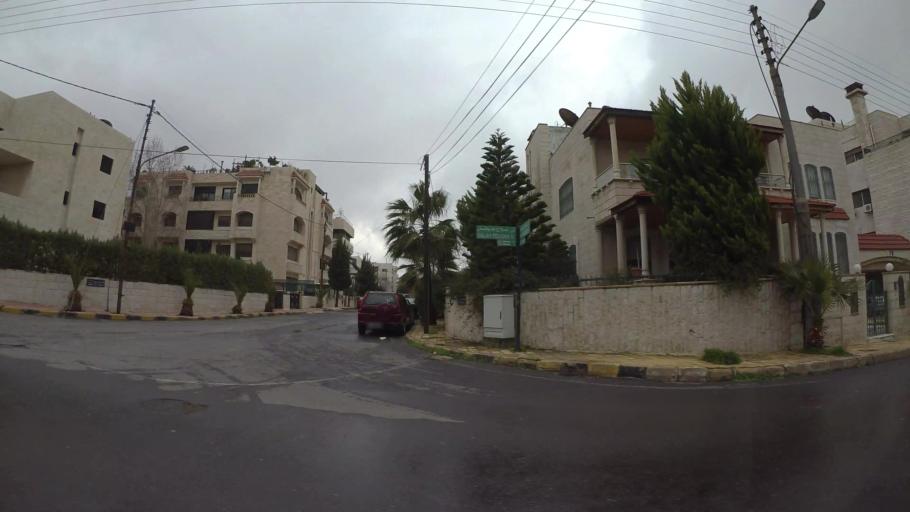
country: JO
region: Amman
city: Wadi as Sir
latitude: 31.9510
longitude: 35.8679
